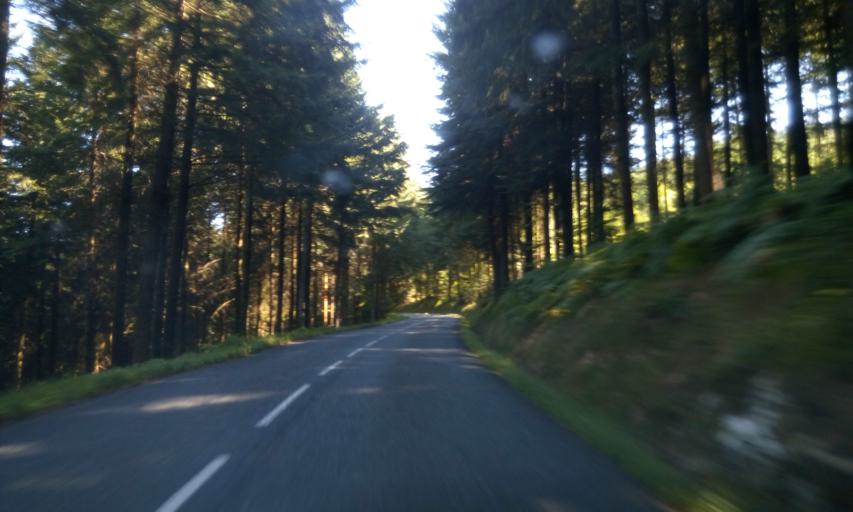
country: FR
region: Rhone-Alpes
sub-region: Departement du Rhone
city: Cublize
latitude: 45.9928
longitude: 4.4110
